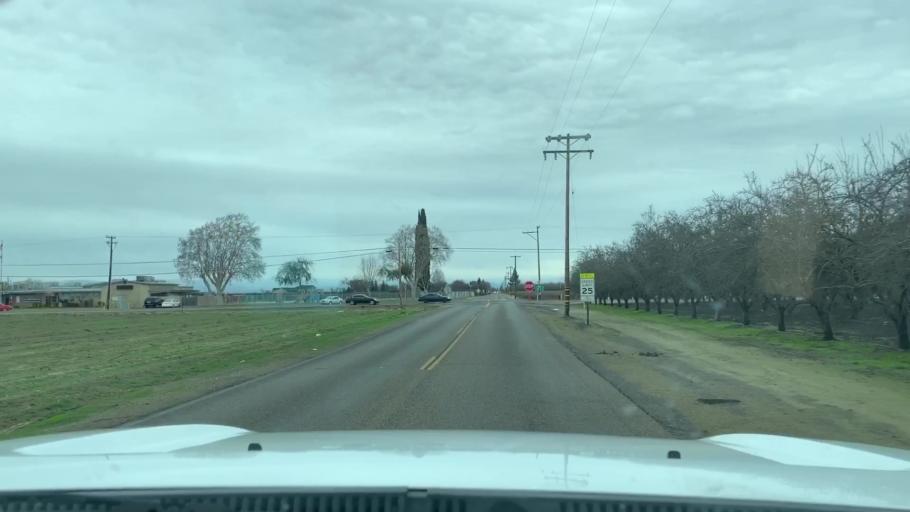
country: US
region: California
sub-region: Fresno County
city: Selma
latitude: 36.5472
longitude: -119.6840
